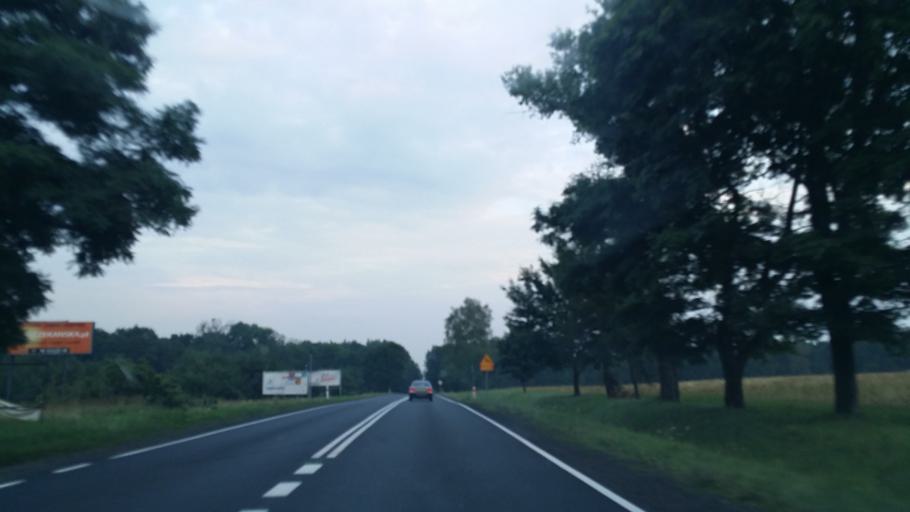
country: PL
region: Lower Silesian Voivodeship
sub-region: Powiat lubinski
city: Osiek
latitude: 51.3665
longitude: 16.2435
